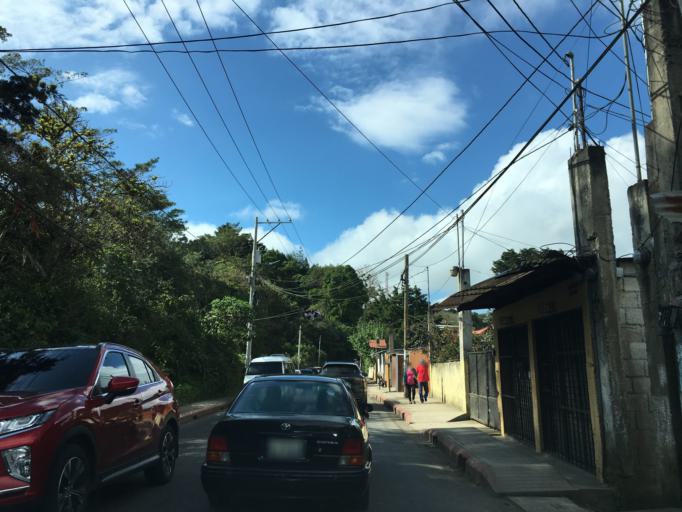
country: GT
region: Guatemala
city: San Jose Pinula
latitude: 14.5637
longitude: -90.4370
